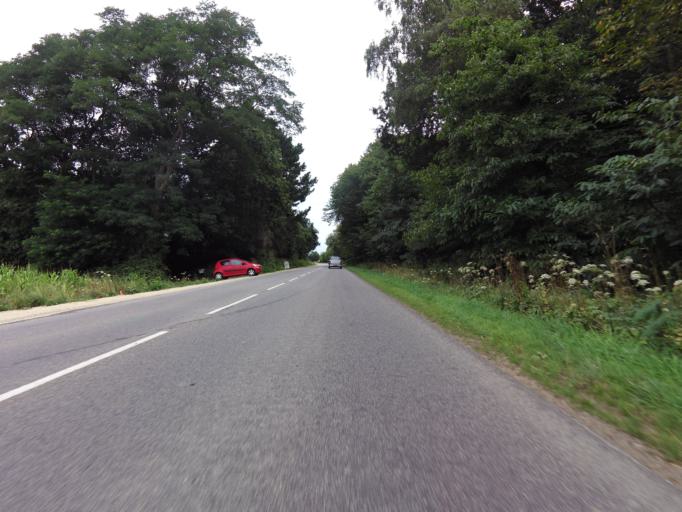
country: FR
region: Brittany
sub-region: Departement du Finistere
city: Douarnenez
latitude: 48.0809
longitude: -4.3618
